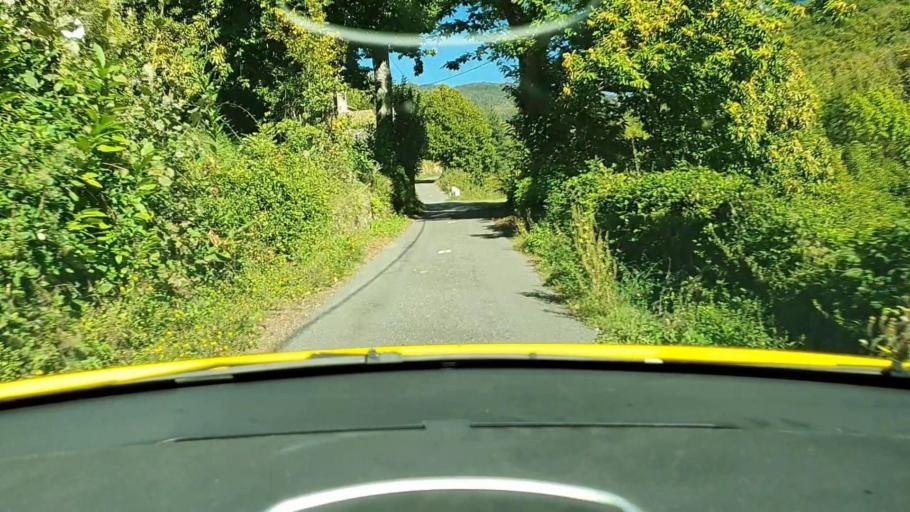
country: FR
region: Languedoc-Roussillon
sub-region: Departement du Gard
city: Le Vigan
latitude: 43.9833
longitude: 3.4455
